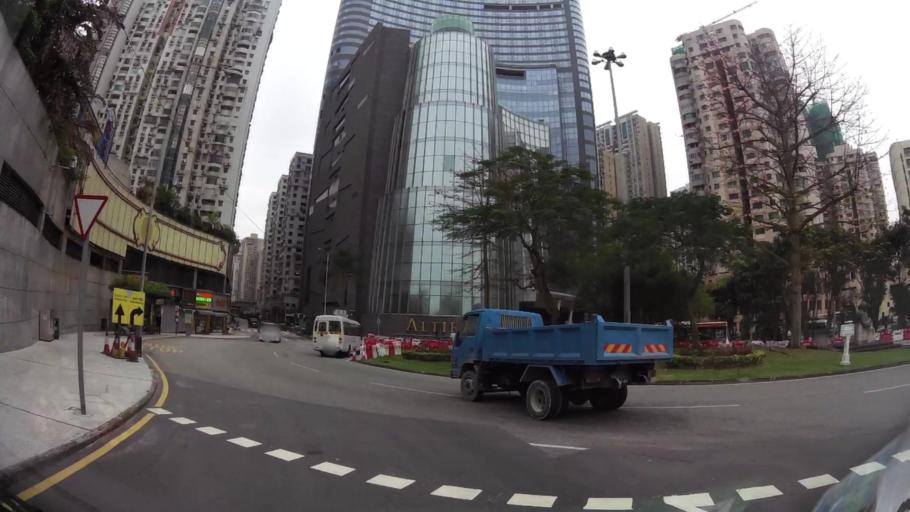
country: MO
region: Macau
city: Macau
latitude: 22.1627
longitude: 113.5548
